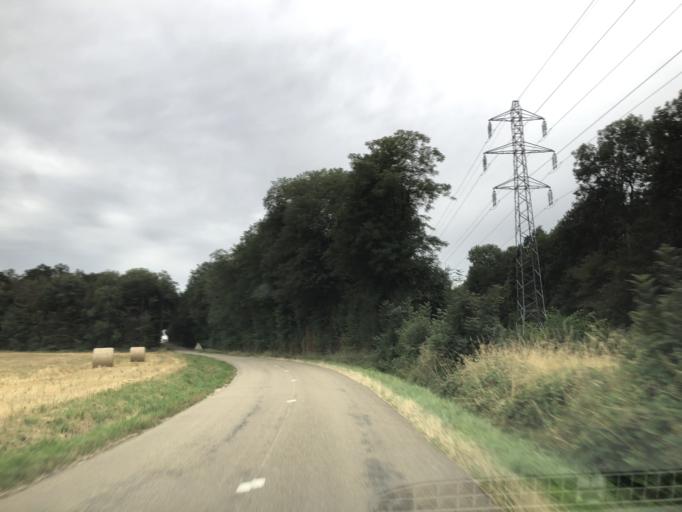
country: FR
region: Centre
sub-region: Departement du Loiret
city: Courtenay
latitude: 47.9954
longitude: 3.1436
